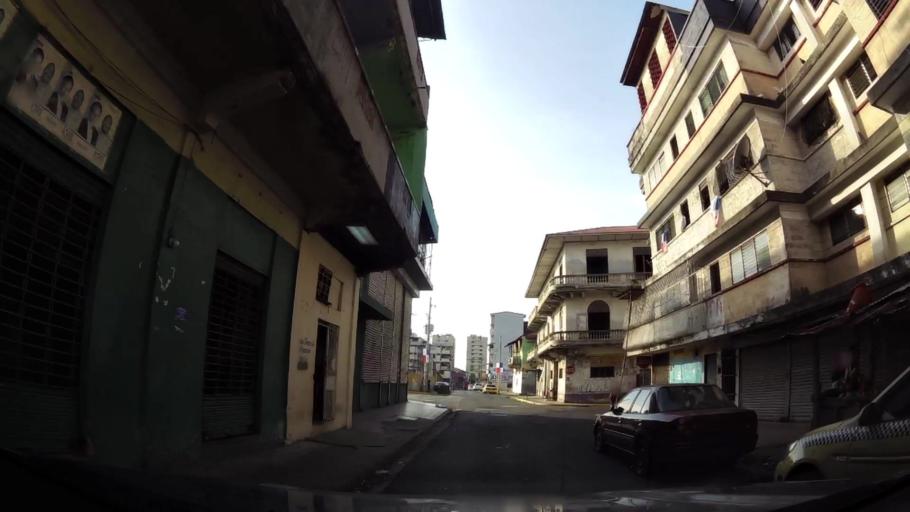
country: PA
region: Panama
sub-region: Distrito de Panama
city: Ancon
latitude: 8.9529
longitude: -79.5413
